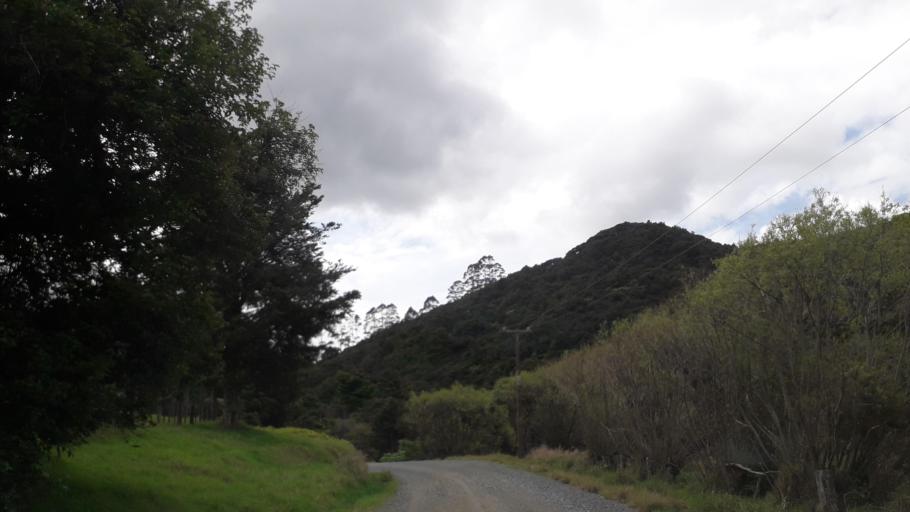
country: NZ
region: Northland
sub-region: Far North District
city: Taipa
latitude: -35.0794
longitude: 173.5554
